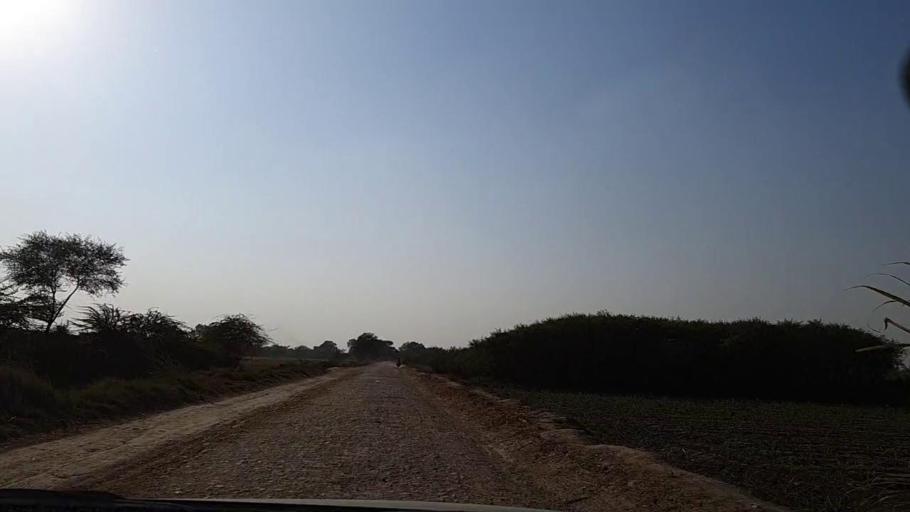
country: PK
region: Sindh
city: Tando Ghulam Ali
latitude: 25.2240
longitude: 68.9488
